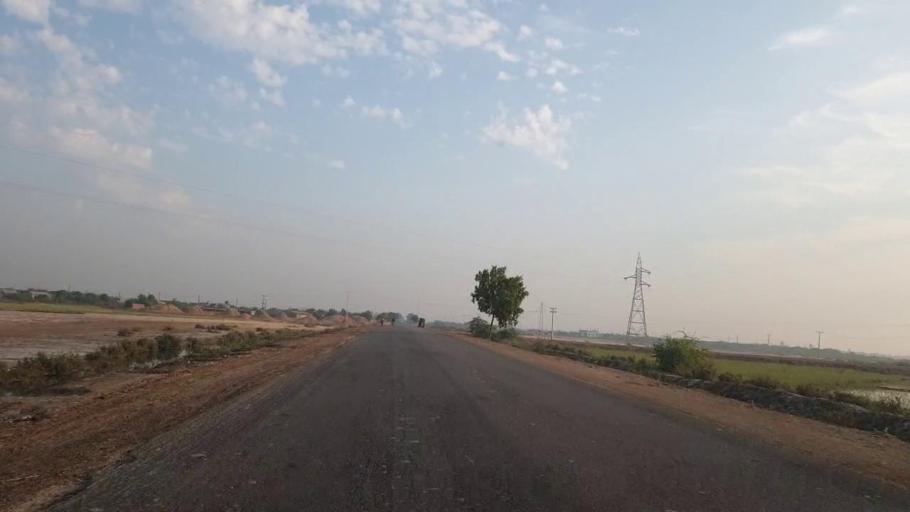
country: PK
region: Sindh
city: Badin
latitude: 24.6862
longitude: 68.9135
